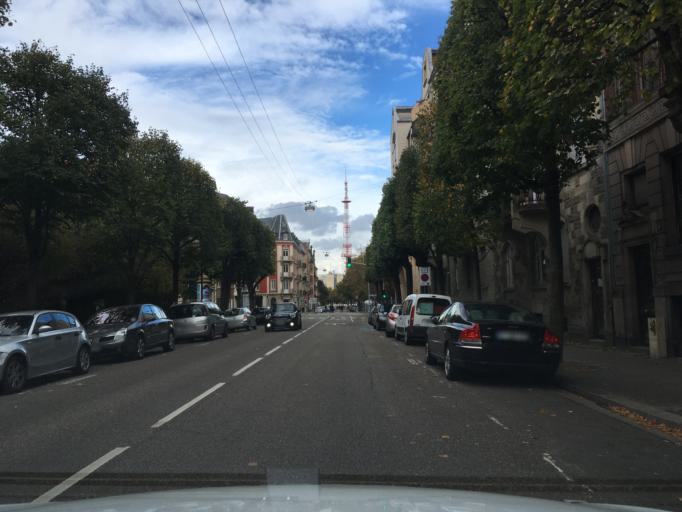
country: FR
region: Alsace
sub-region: Departement du Bas-Rhin
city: Strasbourg
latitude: 48.5916
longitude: 7.7552
